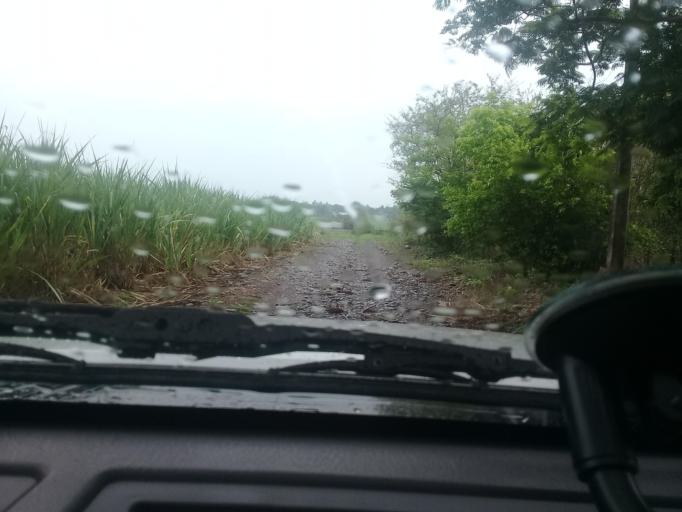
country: MX
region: Veracruz
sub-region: Puente Nacional
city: Cabezas
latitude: 19.3580
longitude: -96.3765
